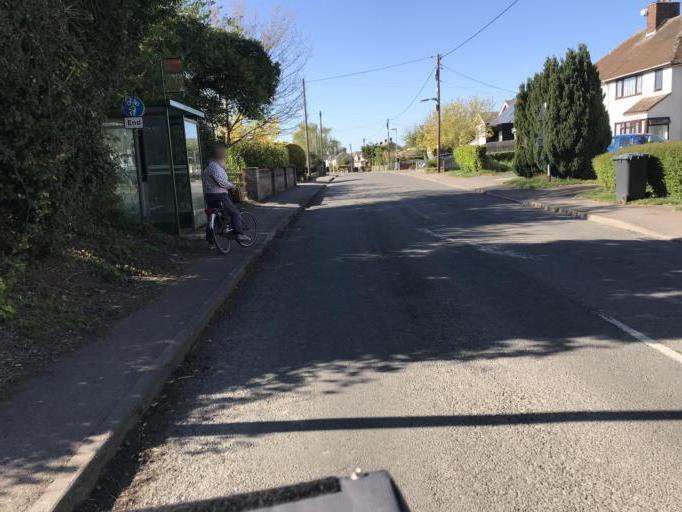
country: GB
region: England
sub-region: Cambridgeshire
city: Fulbourn
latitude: 52.1992
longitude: 0.1952
